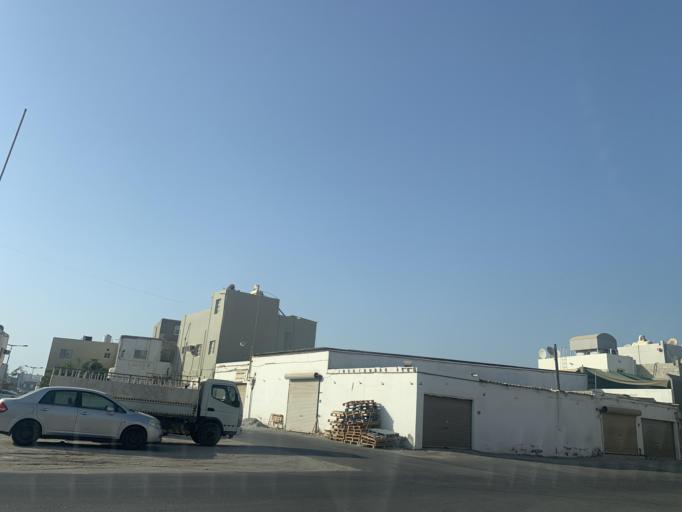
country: BH
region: Muharraq
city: Al Muharraq
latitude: 26.2845
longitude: 50.6323
